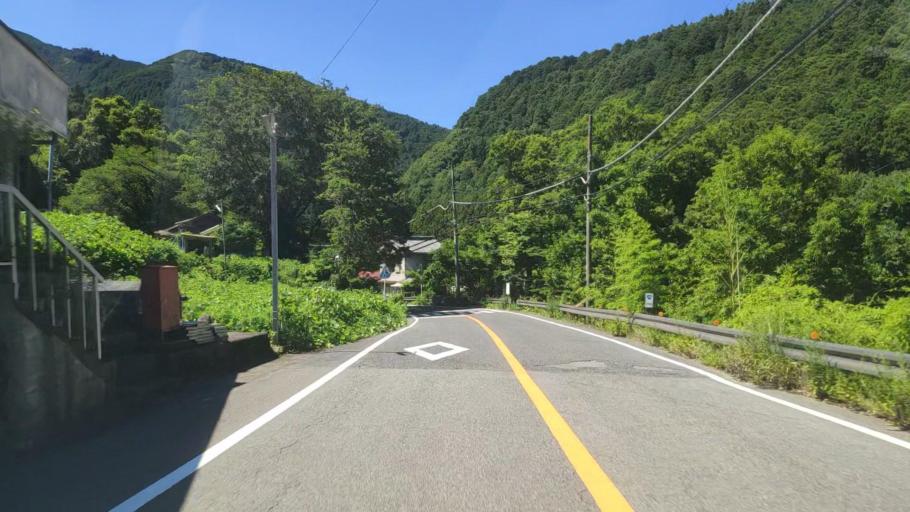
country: JP
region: Nara
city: Yoshino-cho
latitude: 34.2877
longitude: 136.0024
